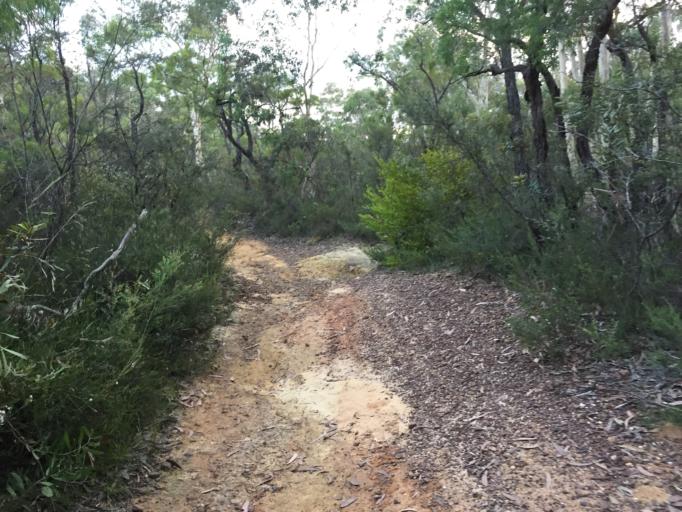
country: AU
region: New South Wales
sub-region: Blue Mountains Municipality
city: Blaxland
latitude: -33.7354
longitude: 150.6197
